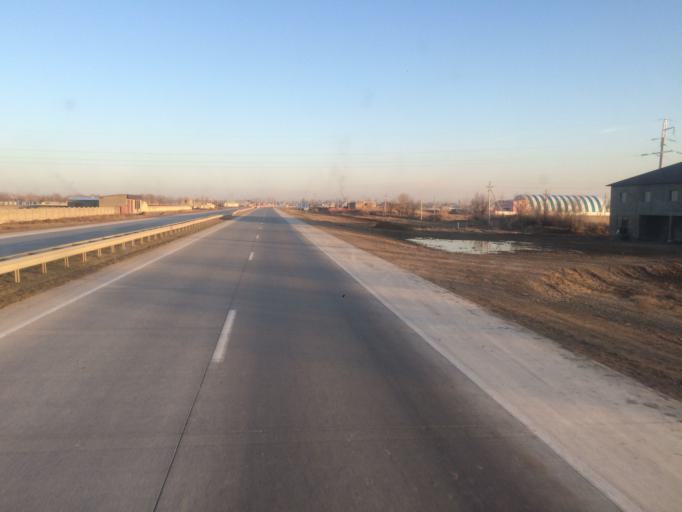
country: KZ
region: Ongtustik Qazaqstan
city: Turkestan
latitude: 43.2663
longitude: 68.3610
